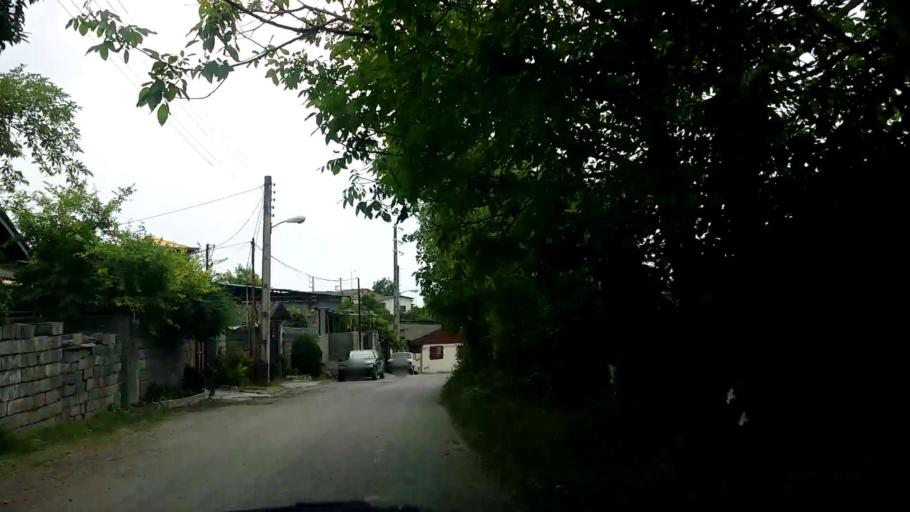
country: IR
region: Mazandaran
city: Chalus
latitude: 36.6537
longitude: 51.4075
